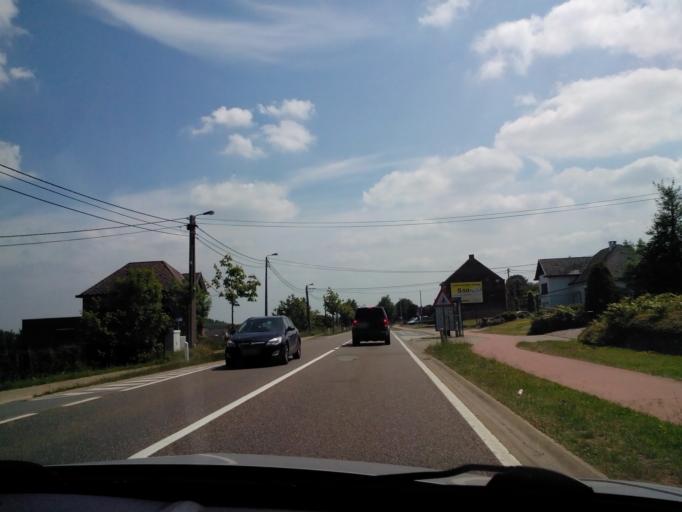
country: BE
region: Flanders
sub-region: Provincie Vlaams-Brabant
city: Aarschot
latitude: 50.9758
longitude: 4.8826
